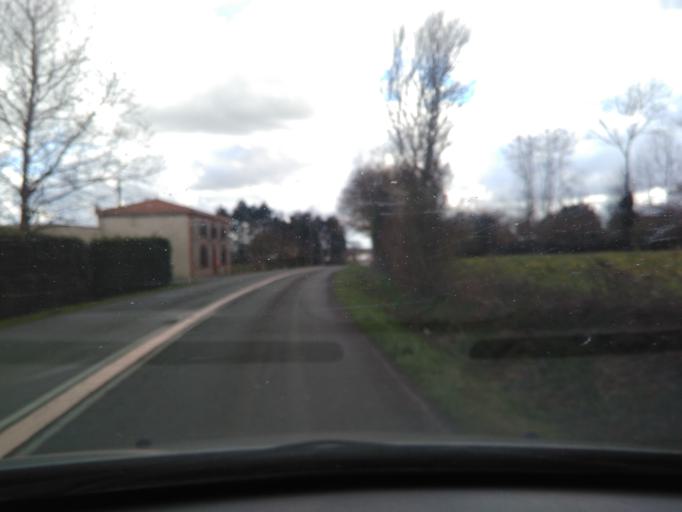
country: FR
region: Pays de la Loire
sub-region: Departement de la Vendee
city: Saint-Martin-des-Noyers
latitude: 46.7361
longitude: -1.1826
